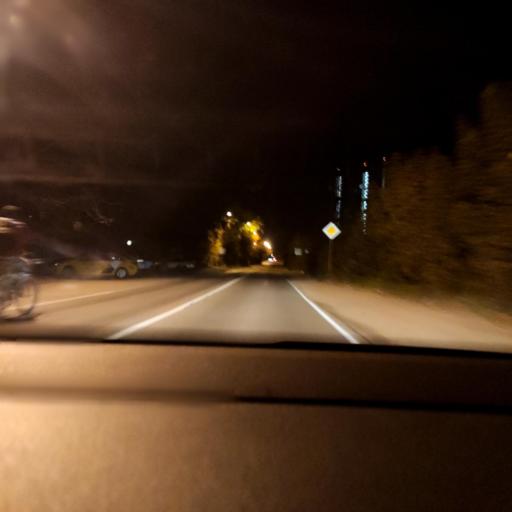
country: RU
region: Moskovskaya
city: Bolshevo
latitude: 55.9436
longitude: 37.8312
